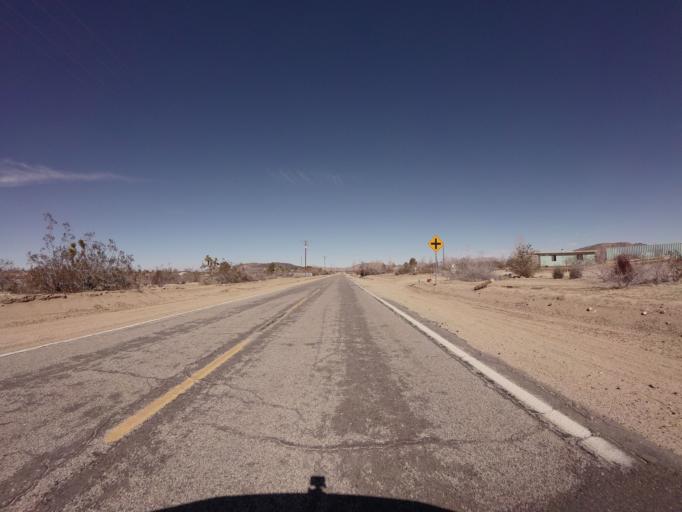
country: US
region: California
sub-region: San Bernardino County
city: Yucca Valley
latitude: 34.2720
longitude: -116.4045
